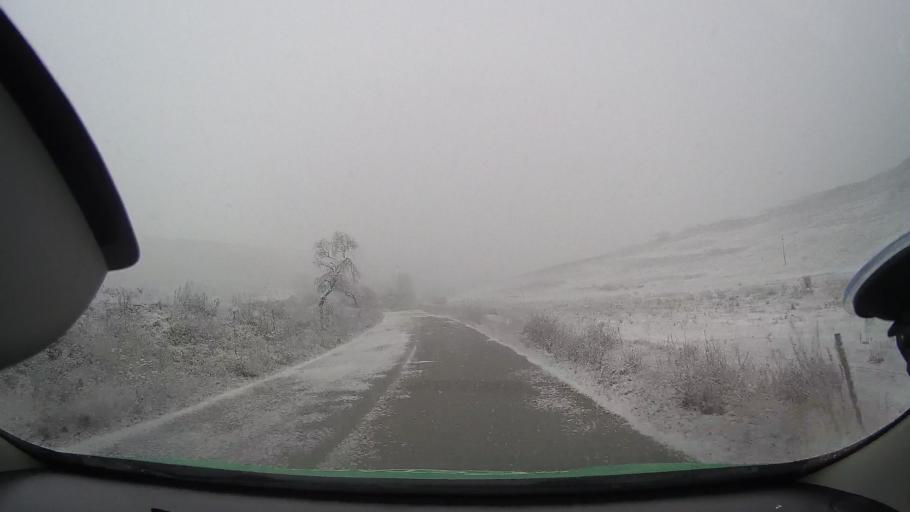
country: RO
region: Alba
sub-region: Comuna Hoparta
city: Hoparta
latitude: 46.3108
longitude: 23.8594
